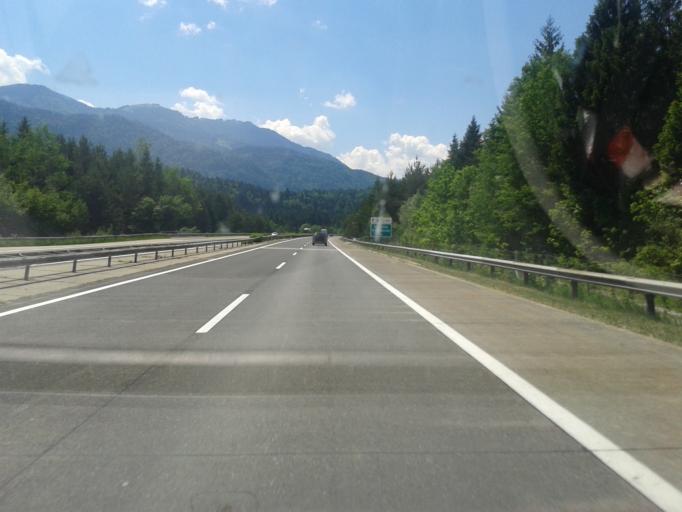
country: AT
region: Carinthia
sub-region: Politischer Bezirk Villach Land
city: Arnoldstein
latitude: 46.5616
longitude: 13.7673
